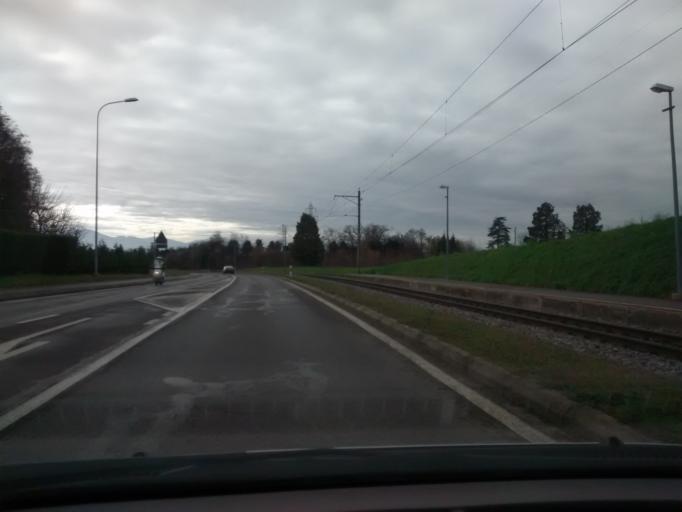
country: CH
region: Vaud
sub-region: Lausanne District
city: Romanel
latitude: 46.5566
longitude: 6.6011
